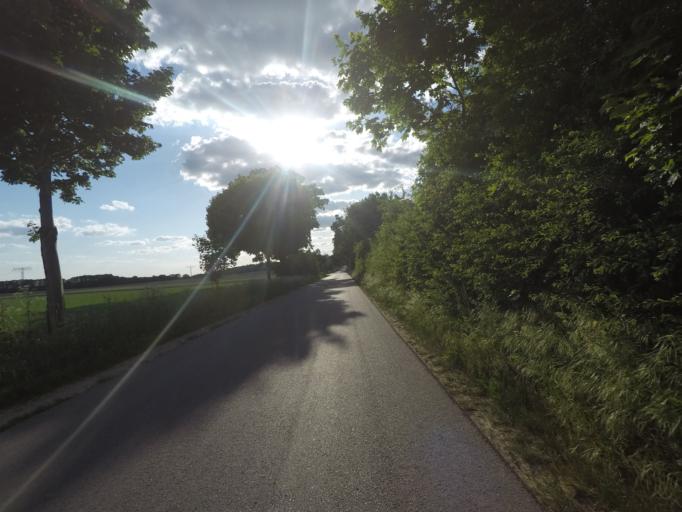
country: DE
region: Brandenburg
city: Britz
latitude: 52.8910
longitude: 13.7917
